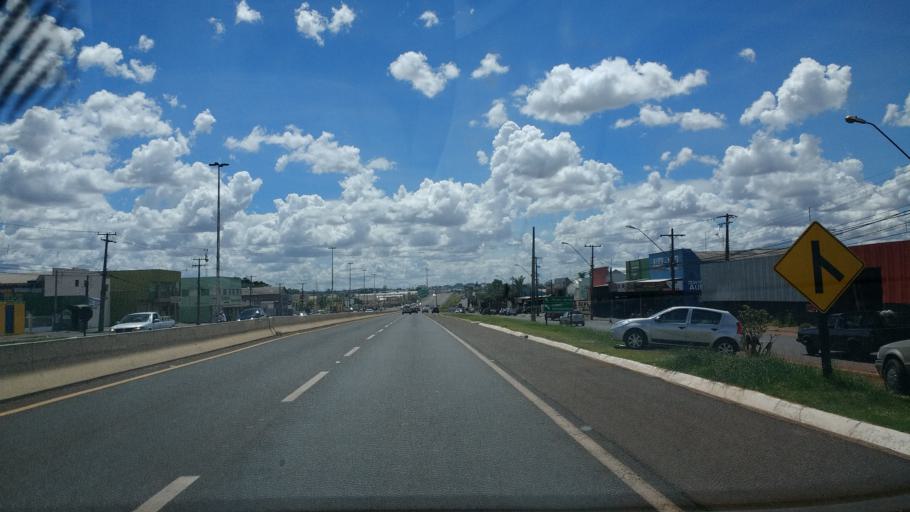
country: BR
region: Parana
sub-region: Londrina
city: Londrina
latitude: -23.3090
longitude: -51.2195
